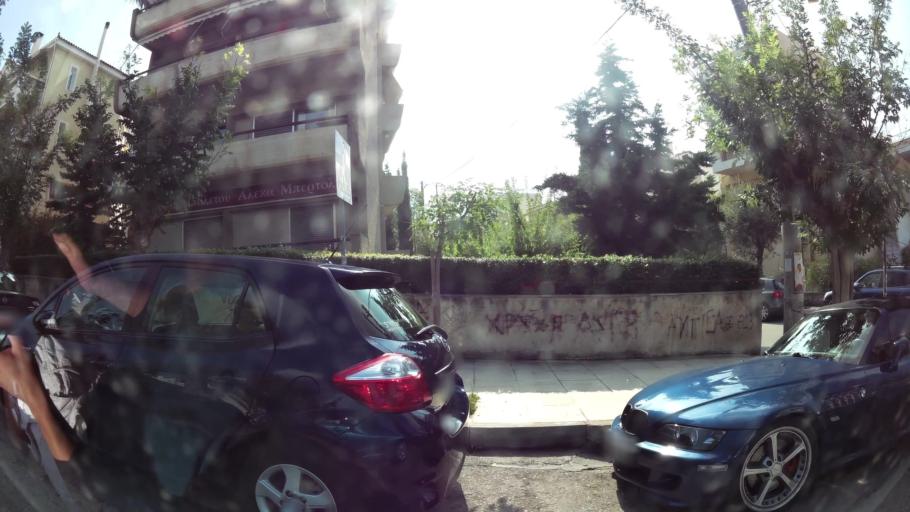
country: GR
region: Attica
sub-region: Nomarchia Athinas
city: Papagou
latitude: 37.9922
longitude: 23.7983
